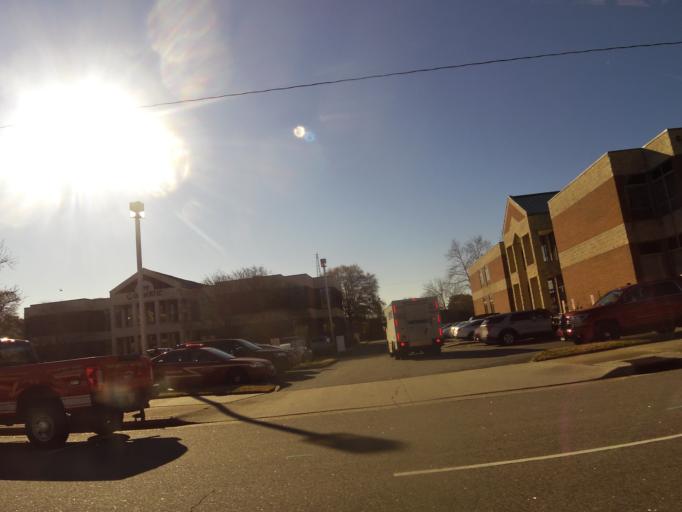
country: US
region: Virginia
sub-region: City of Portsmouth
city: Portsmouth
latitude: 36.8338
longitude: -76.2999
